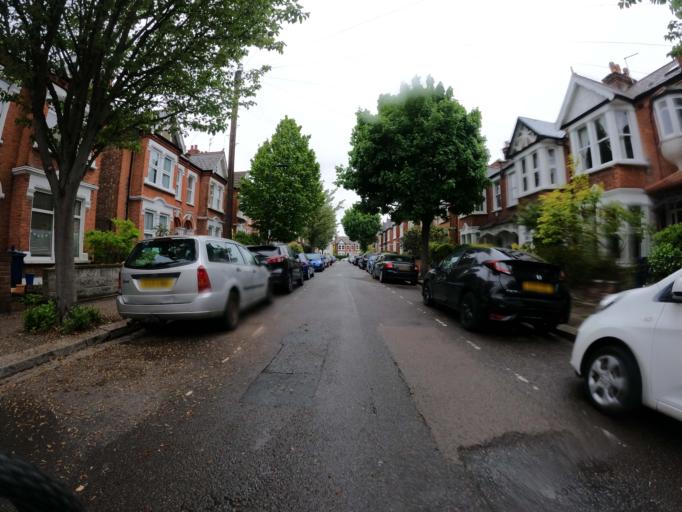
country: GB
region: England
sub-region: Greater London
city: Acton
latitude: 51.5092
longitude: -0.2705
